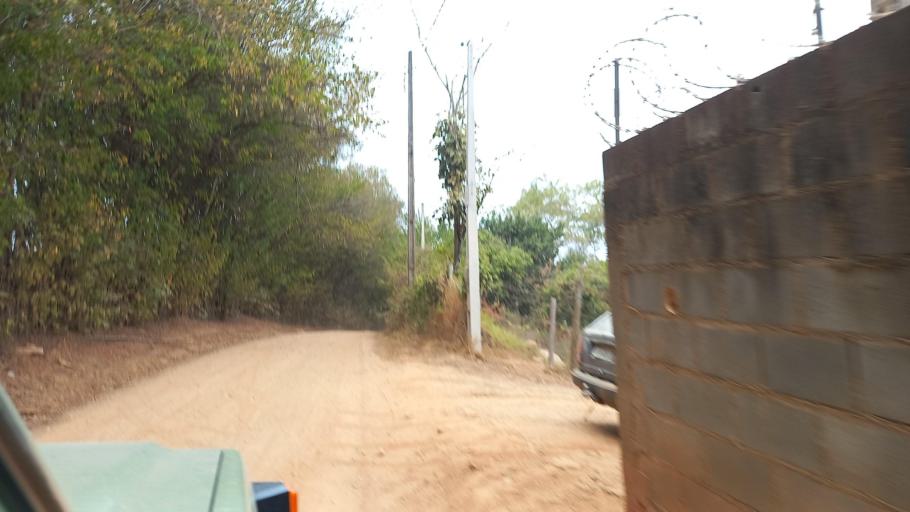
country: BR
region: Sao Paulo
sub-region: Moji-Guacu
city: Mogi-Gaucu
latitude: -22.2950
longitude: -46.8317
